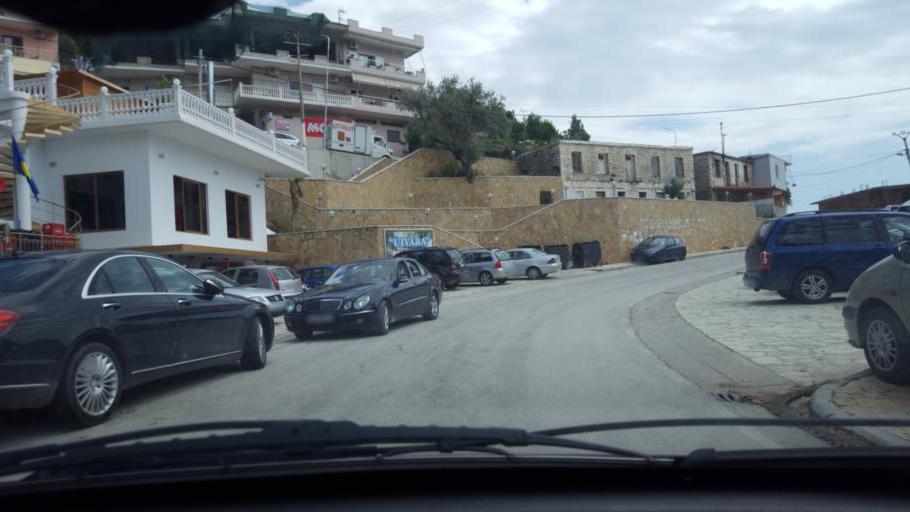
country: AL
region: Vlore
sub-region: Rrethi i Sarandes
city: Lukove
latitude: 40.0617
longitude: 19.8577
